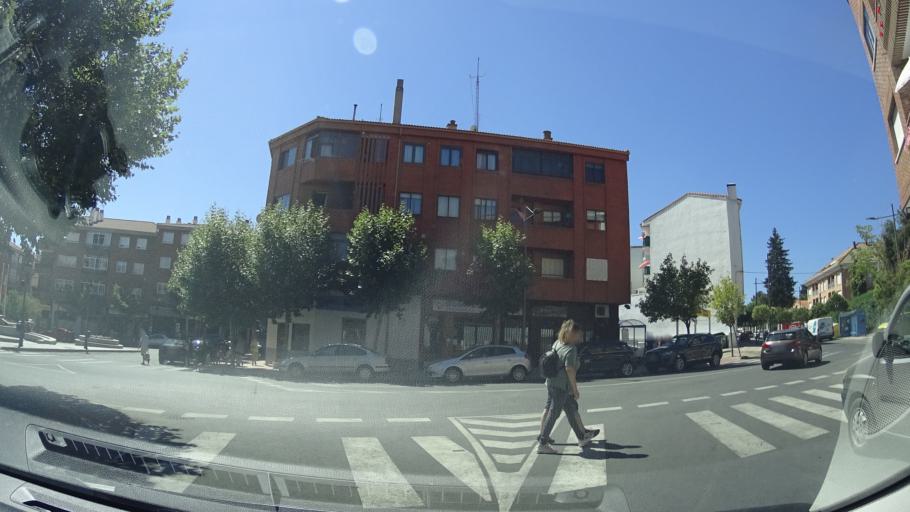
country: ES
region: Castille and Leon
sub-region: Provincia de Avila
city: Las Navas del Marques
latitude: 40.6026
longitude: -4.3348
